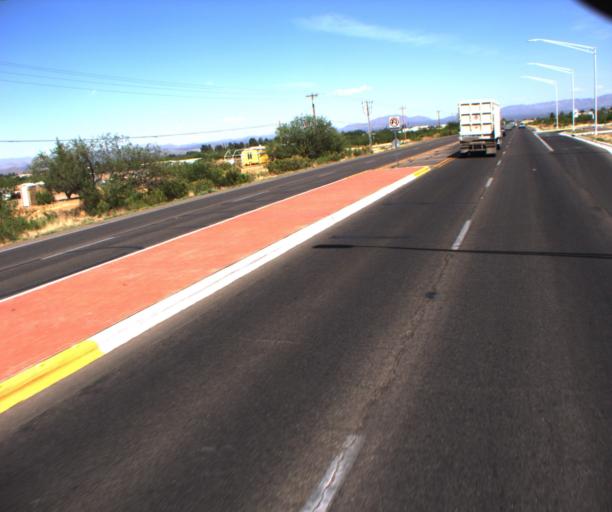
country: US
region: Arizona
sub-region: Cochise County
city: Sierra Vista
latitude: 31.5546
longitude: -110.2297
